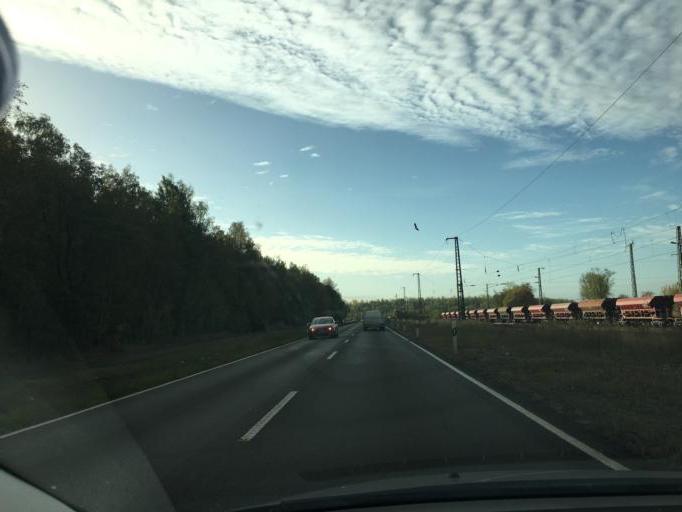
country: DE
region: Saxony
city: Neukieritzsch
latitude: 51.1451
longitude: 12.4167
